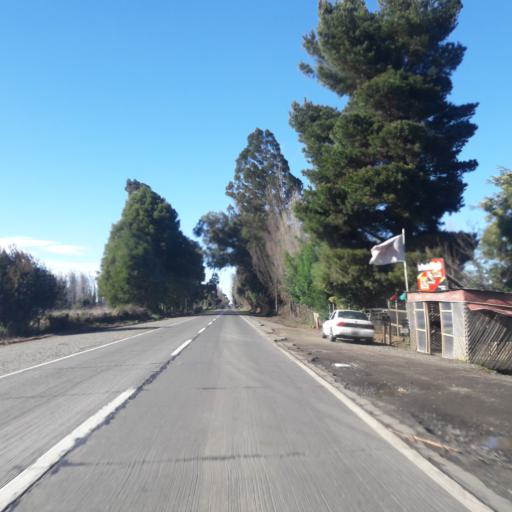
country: CL
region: Araucania
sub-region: Provincia de Malleco
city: Angol
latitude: -37.7613
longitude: -72.5688
